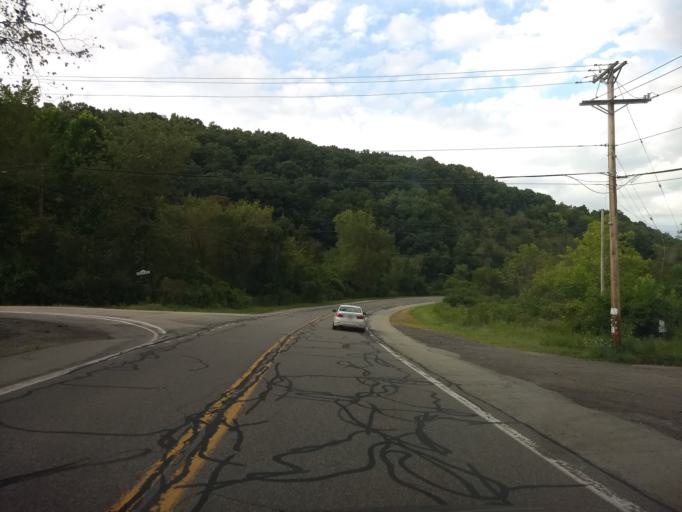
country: US
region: Pennsylvania
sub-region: Allegheny County
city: Coraopolis
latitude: 40.4609
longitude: -80.1688
